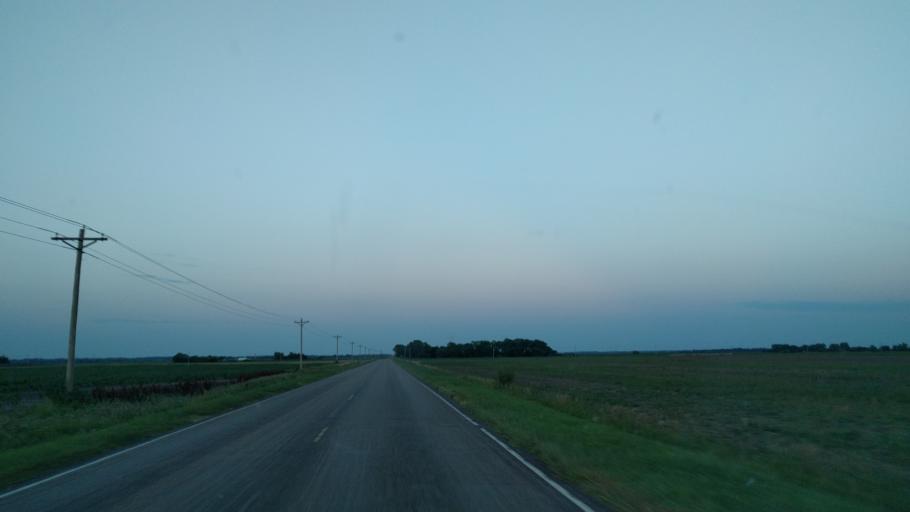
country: US
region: Kansas
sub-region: Reno County
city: Nickerson
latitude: 38.2176
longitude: -98.1134
